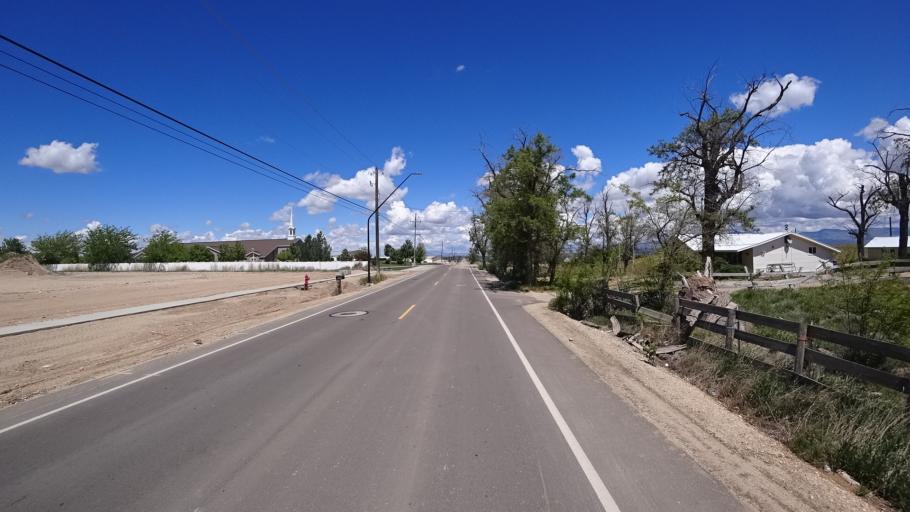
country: US
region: Idaho
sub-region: Ada County
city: Meridian
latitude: 43.5431
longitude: -116.3543
